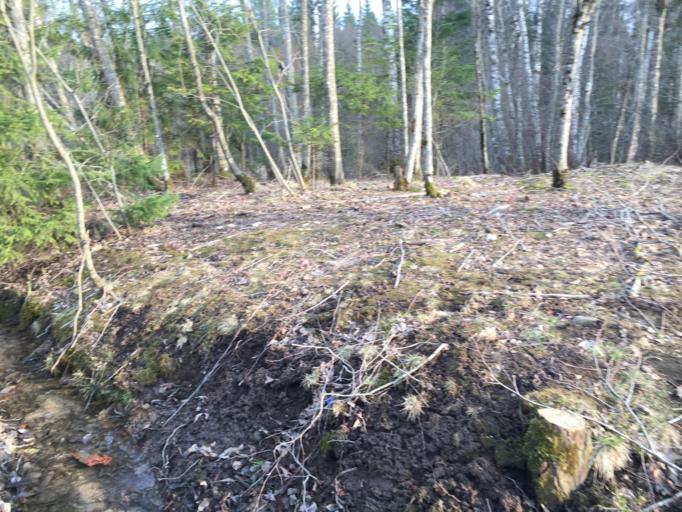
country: LV
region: Raunas
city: Rauna
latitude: 57.1572
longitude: 25.5710
